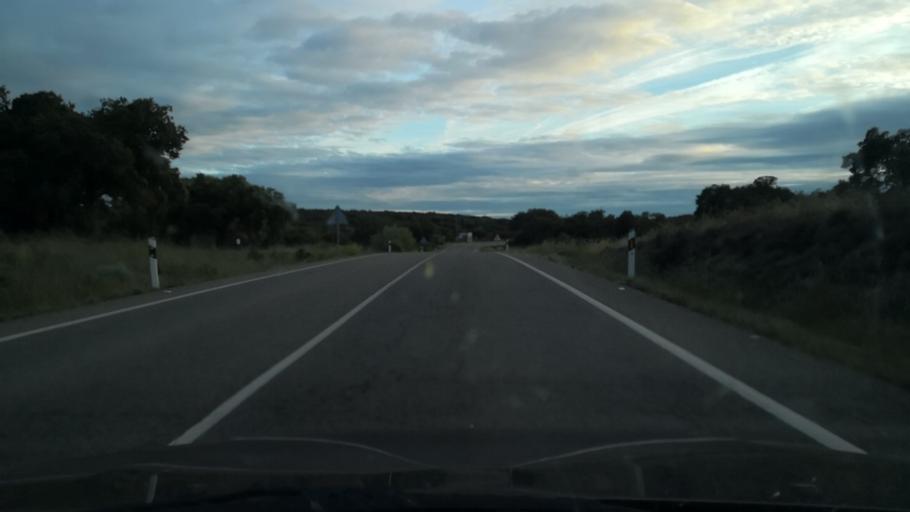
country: ES
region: Extremadura
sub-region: Provincia de Badajoz
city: La Roca de la Sierra
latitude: 39.1400
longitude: -6.6553
